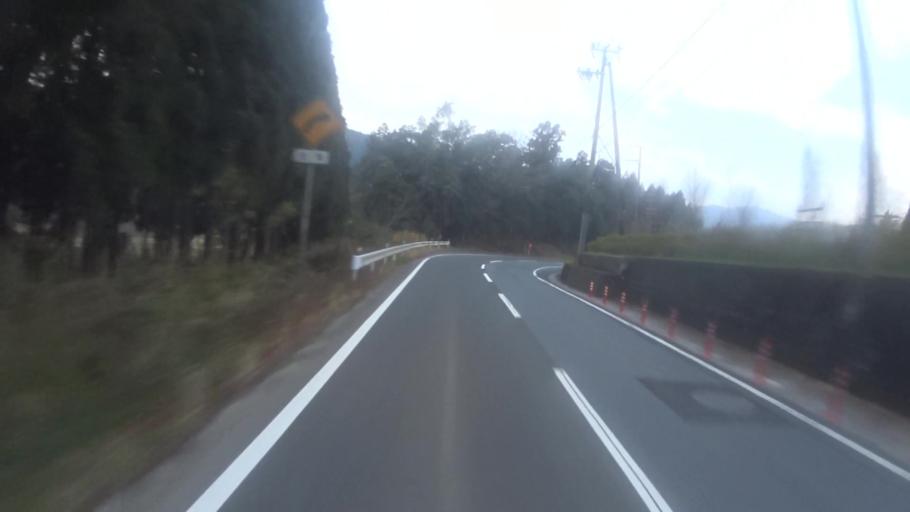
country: JP
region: Kyoto
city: Ayabe
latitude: 35.3056
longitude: 135.3150
